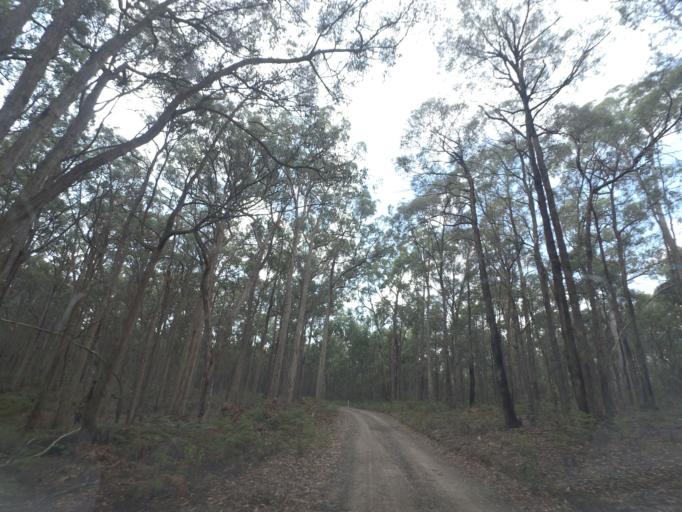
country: AU
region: Victoria
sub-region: Moorabool
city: Bacchus Marsh
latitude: -37.4543
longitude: 144.3564
